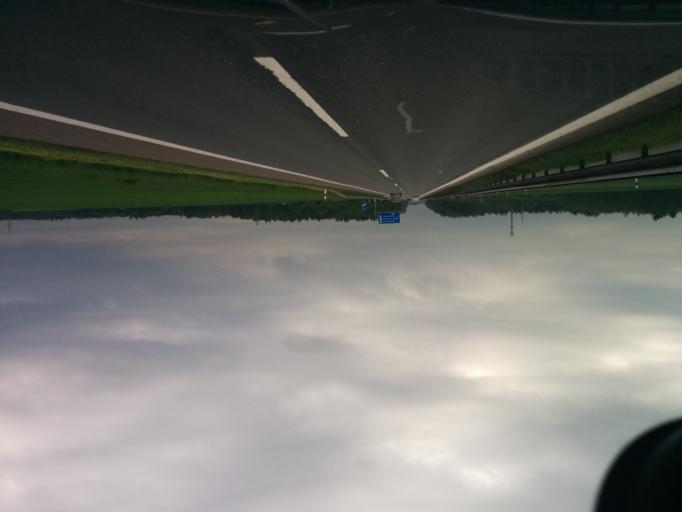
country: DE
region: Bavaria
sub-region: Upper Bavaria
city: Ottobrunn
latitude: 48.0456
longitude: 11.6483
